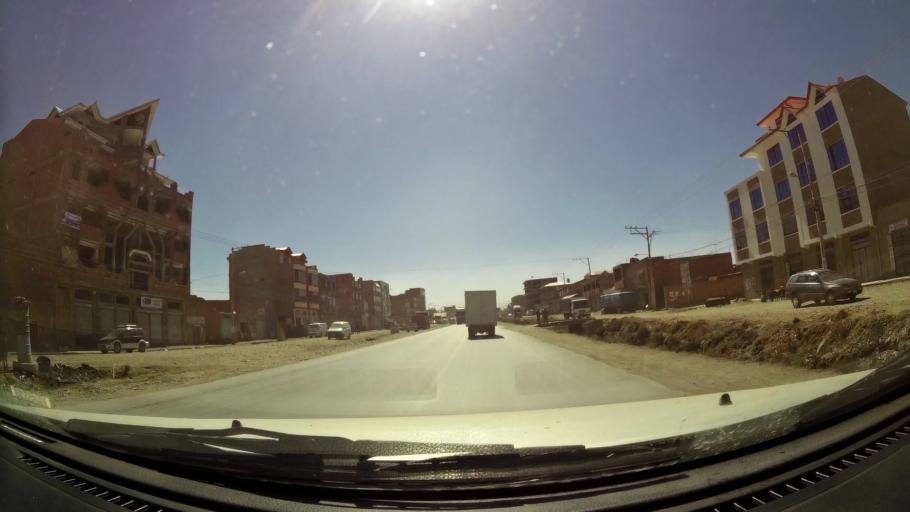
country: BO
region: La Paz
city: La Paz
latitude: -16.5524
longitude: -68.2071
